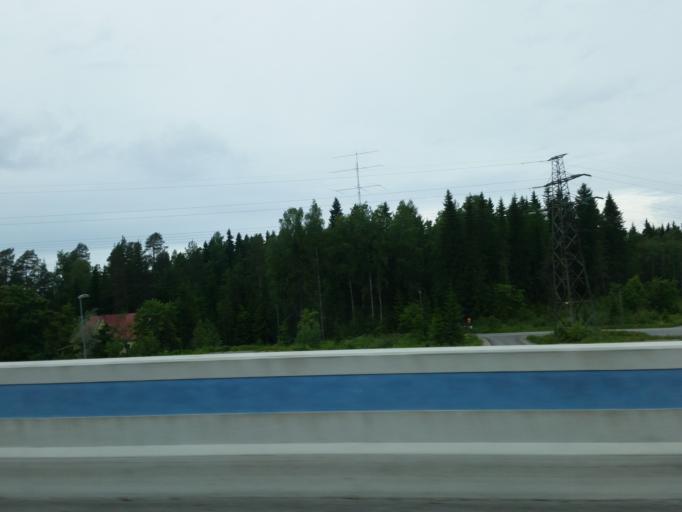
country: FI
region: Northern Savo
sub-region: Kuopio
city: Kuopio
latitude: 62.9506
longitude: 27.6758
